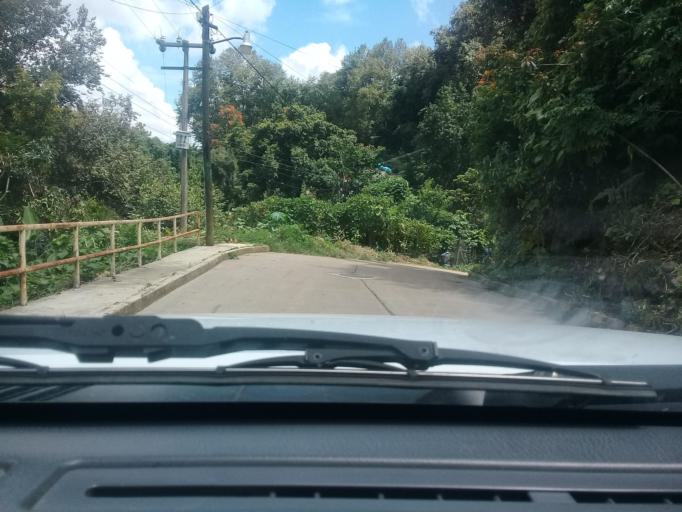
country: MX
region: Veracruz
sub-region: Tlalnelhuayocan
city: Otilpan
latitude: 19.5375
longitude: -96.9724
